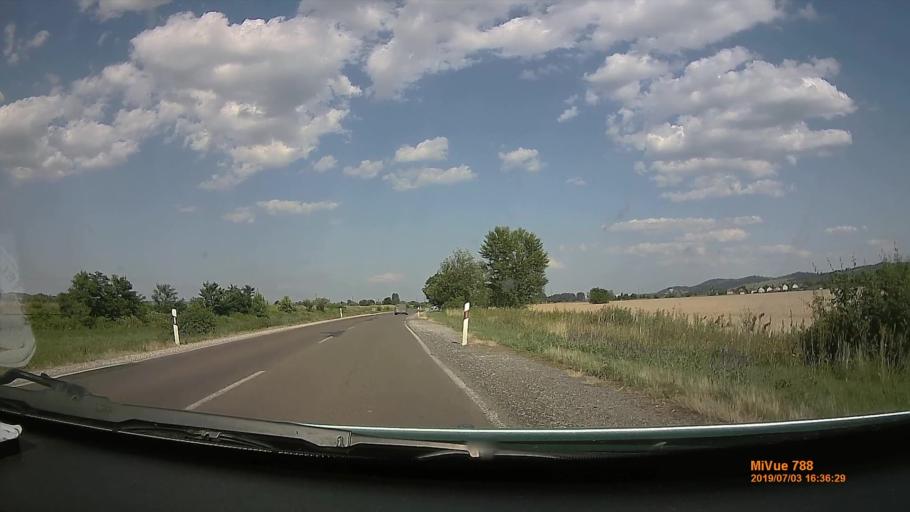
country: HU
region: Borsod-Abauj-Zemplen
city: Sajokaza
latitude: 48.2743
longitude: 20.5694
